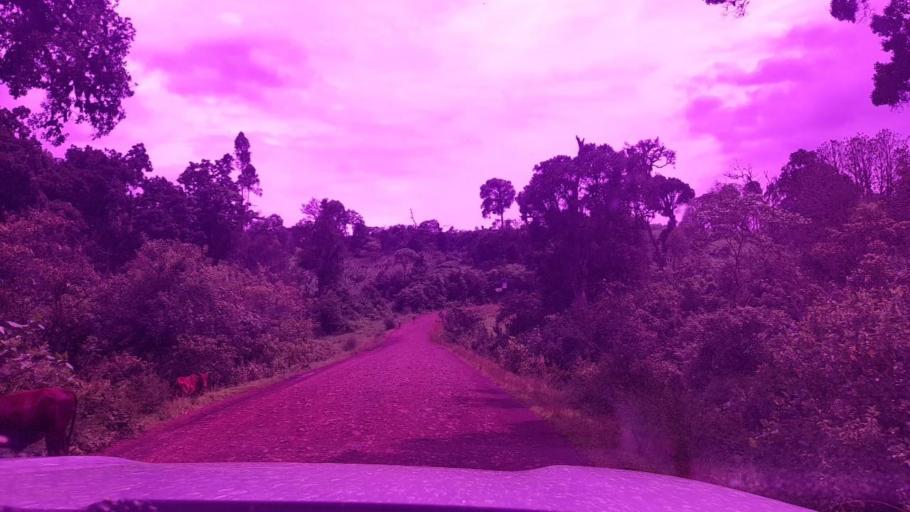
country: ET
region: Southern Nations, Nationalities, and People's Region
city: Tippi
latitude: 7.6322
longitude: 35.5667
